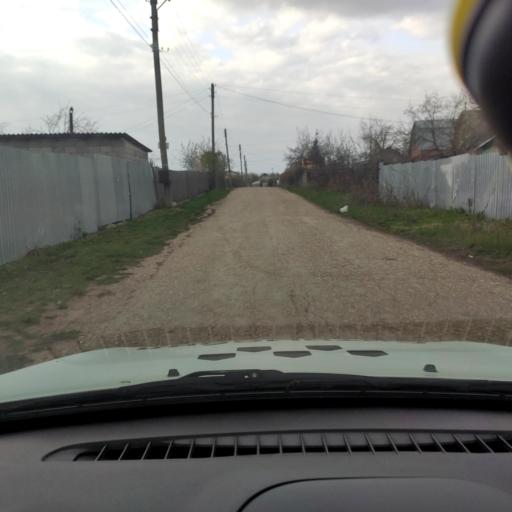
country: RU
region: Samara
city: Mezhdurechensk
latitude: 53.2464
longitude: 49.1478
